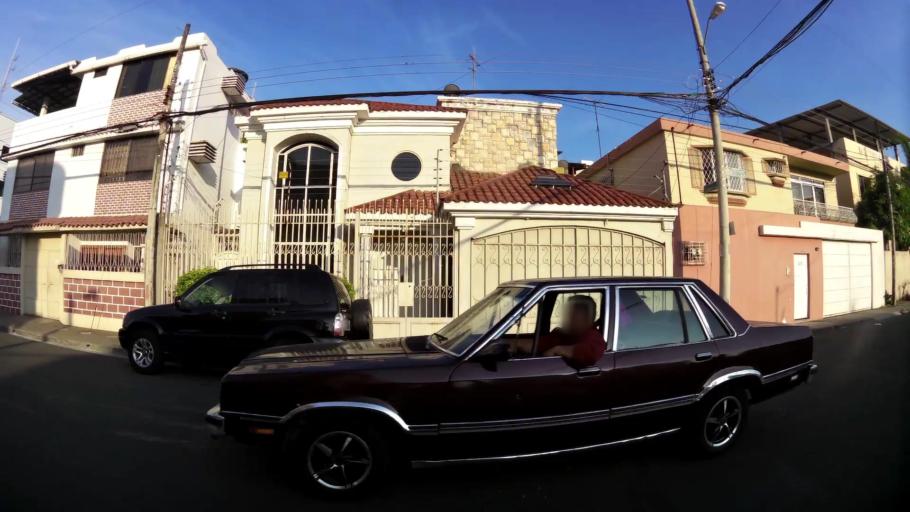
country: EC
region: Guayas
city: Eloy Alfaro
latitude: -2.1598
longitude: -79.8945
